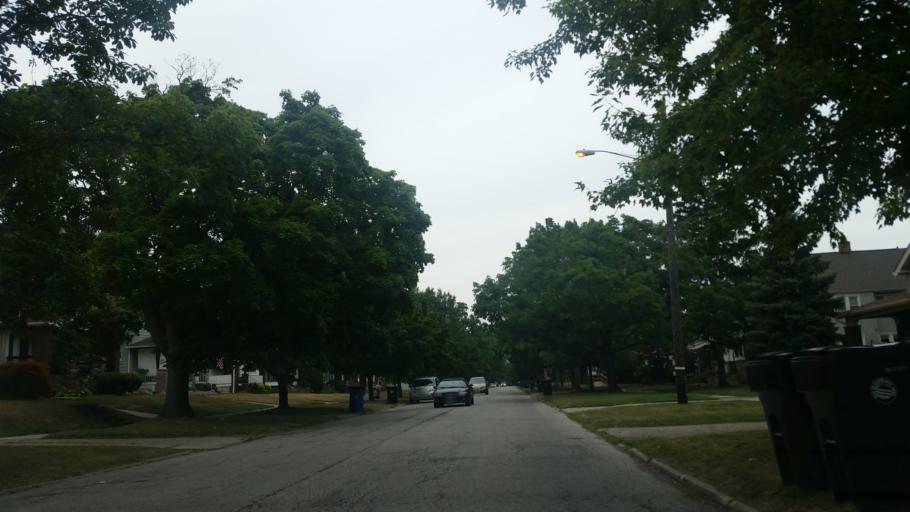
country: US
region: Ohio
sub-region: Cuyahoga County
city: Brooklyn Heights
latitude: 41.4266
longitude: -81.6985
